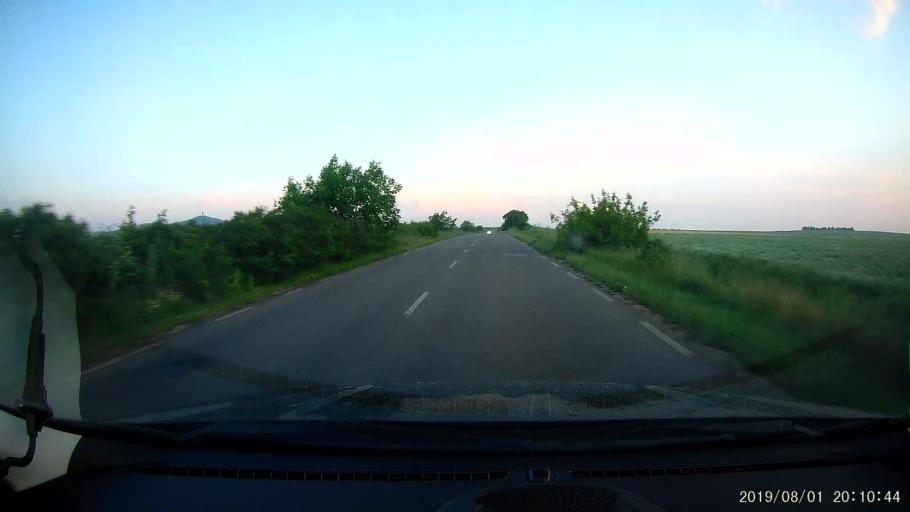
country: BG
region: Yambol
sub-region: Obshtina Yambol
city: Yambol
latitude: 42.4756
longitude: 26.6021
